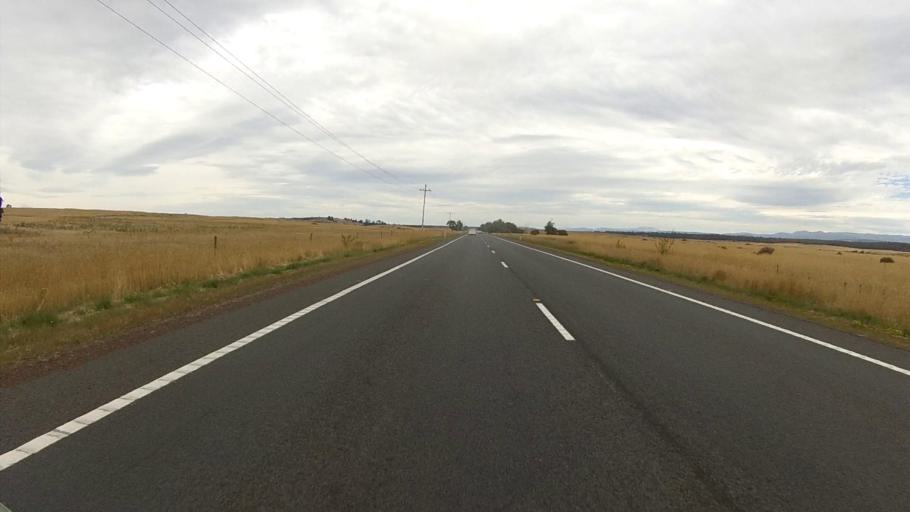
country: AU
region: Tasmania
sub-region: Northern Midlands
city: Evandale
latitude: -41.8955
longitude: 147.4732
